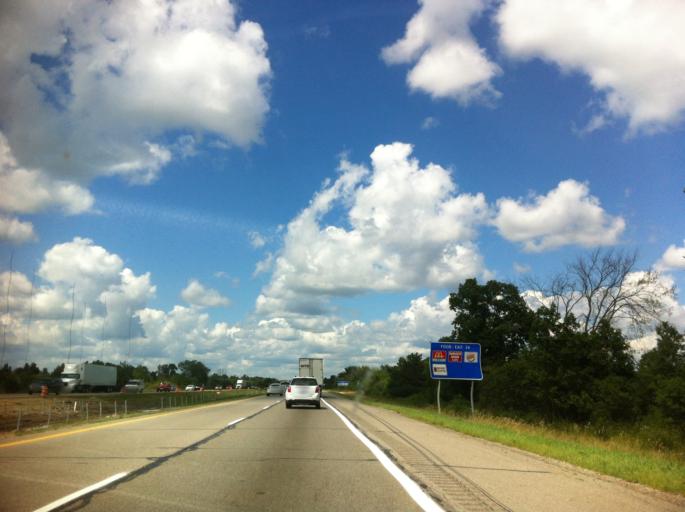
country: US
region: Michigan
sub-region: Washtenaw County
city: Ypsilanti
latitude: 42.1887
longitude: -83.6845
